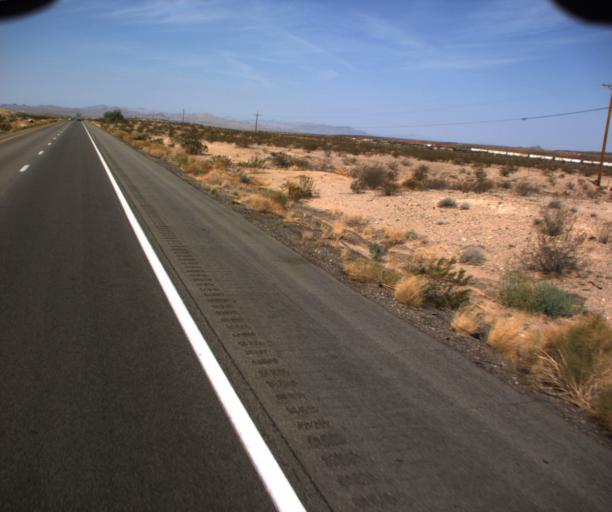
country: US
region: Arizona
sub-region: Mohave County
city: Desert Hills
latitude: 34.7702
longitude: -114.1955
